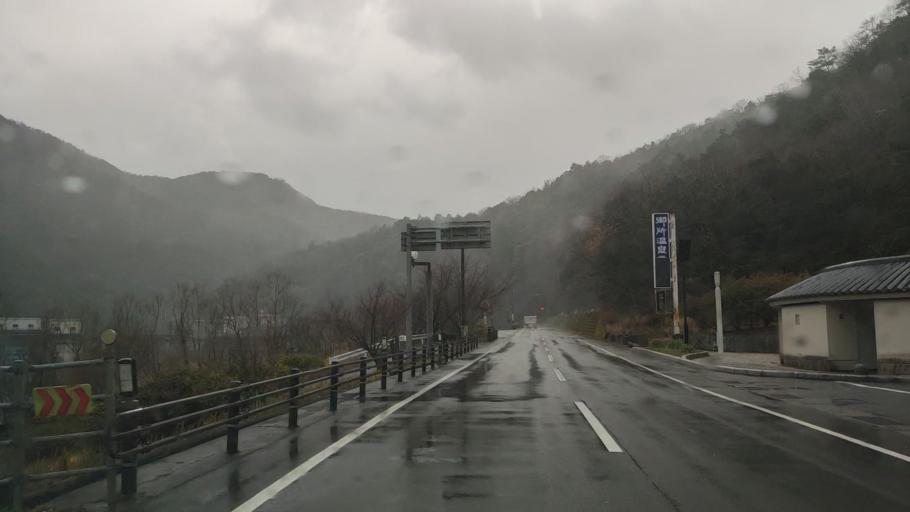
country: JP
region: Tokushima
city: Kamojimacho-jogejima
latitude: 34.1499
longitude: 134.3528
